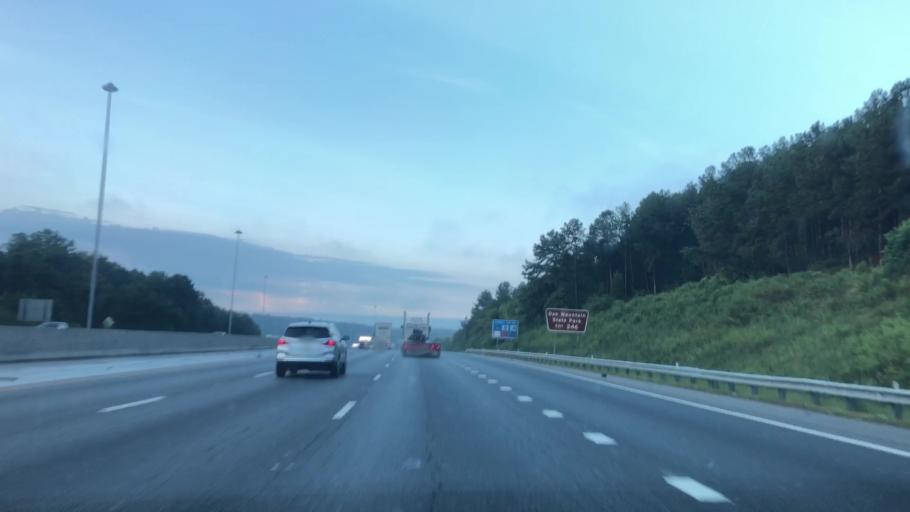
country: US
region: Alabama
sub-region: Shelby County
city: Indian Springs Village
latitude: 33.3488
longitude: -86.7806
